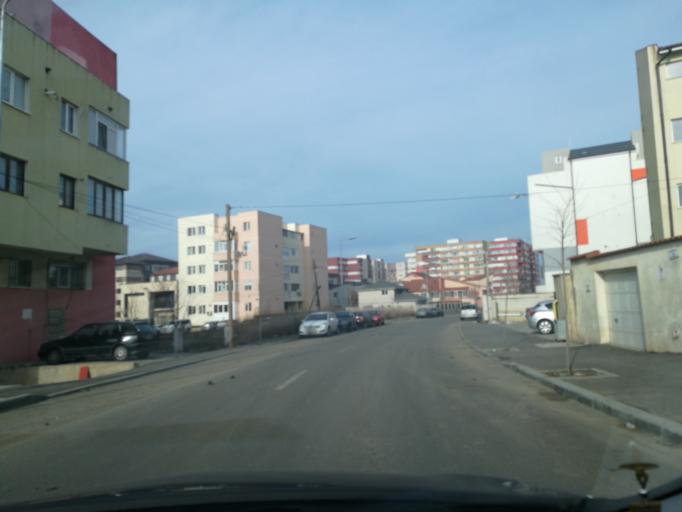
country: RO
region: Constanta
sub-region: Municipiul Constanta
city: Constanta
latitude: 44.1852
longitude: 28.6112
